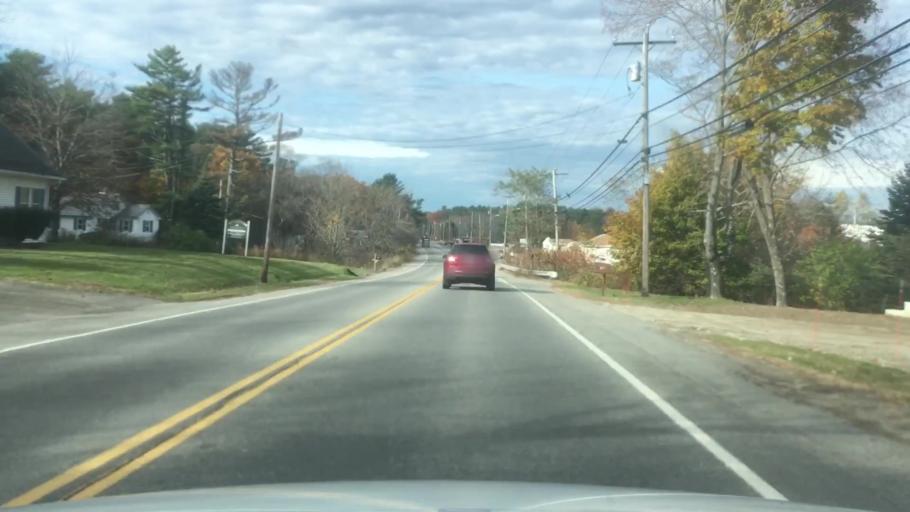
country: US
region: Maine
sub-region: Sagadahoc County
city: Bath
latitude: 43.9128
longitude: -69.8787
